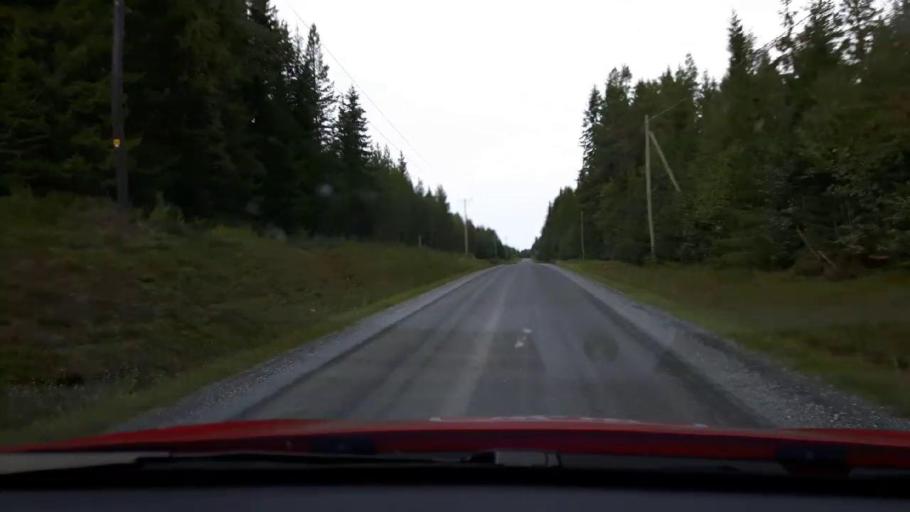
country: SE
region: Jaemtland
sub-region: Krokoms Kommun
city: Valla
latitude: 63.2468
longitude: 13.9644
